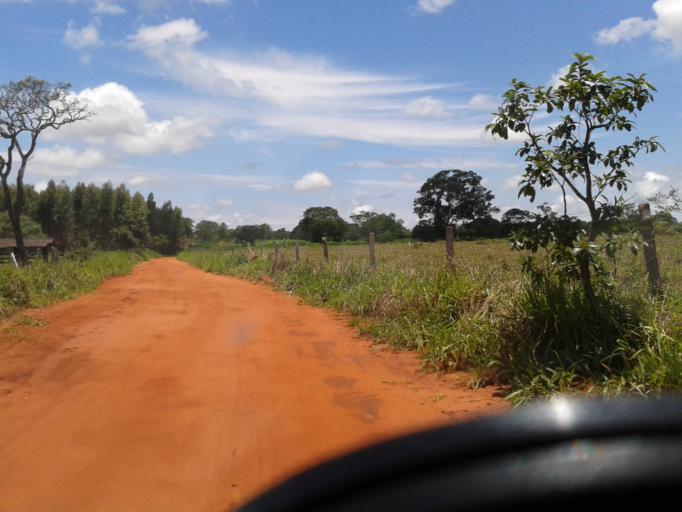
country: BR
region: Minas Gerais
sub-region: Santa Vitoria
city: Santa Vitoria
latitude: -18.9333
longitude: -49.8566
